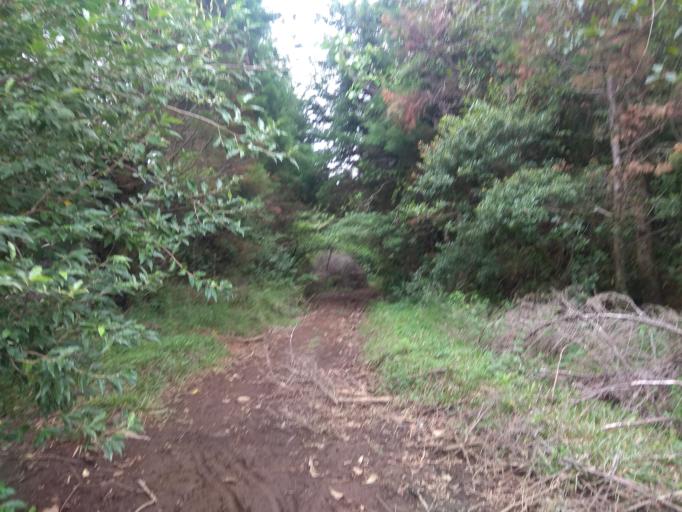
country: CR
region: Heredia
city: San Josecito
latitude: 10.0726
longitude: -84.0832
